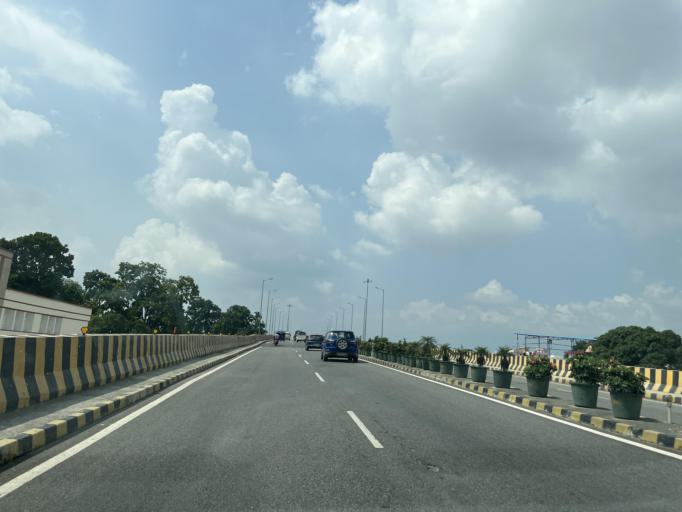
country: IN
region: Uttarakhand
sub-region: Dehradun
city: Raipur
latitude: 30.2759
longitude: 78.0754
